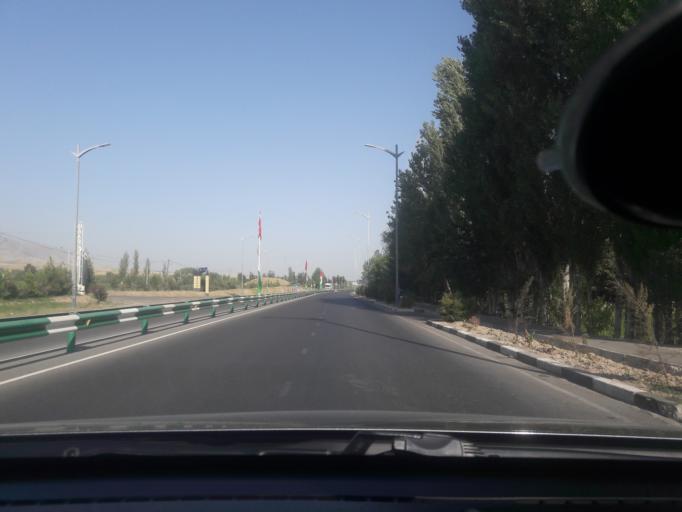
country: TJ
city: Shahrinav
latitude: 38.5763
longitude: 68.3393
